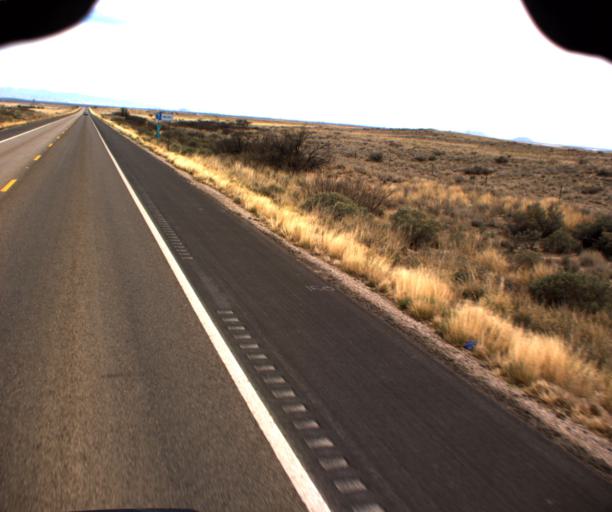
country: US
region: Arizona
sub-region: Cochise County
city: Willcox
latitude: 32.2271
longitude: -109.7974
